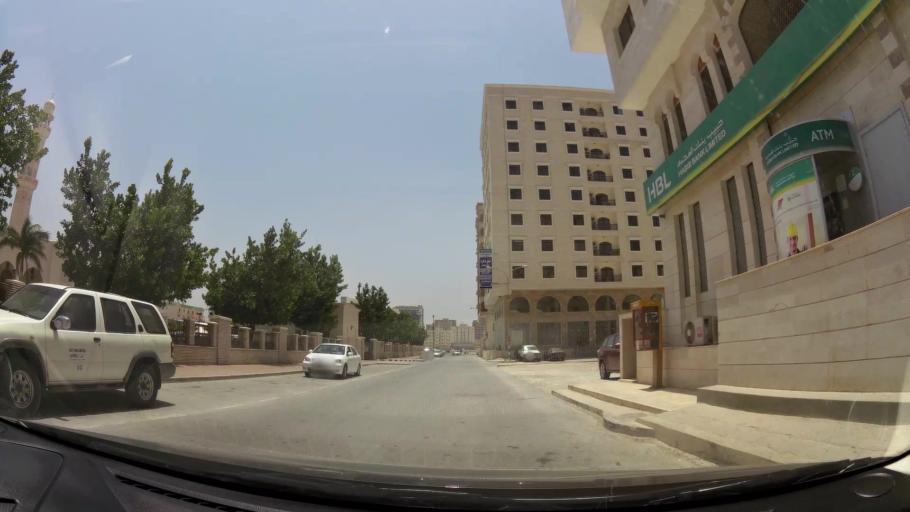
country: OM
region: Zufar
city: Salalah
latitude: 17.0171
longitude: 54.0949
